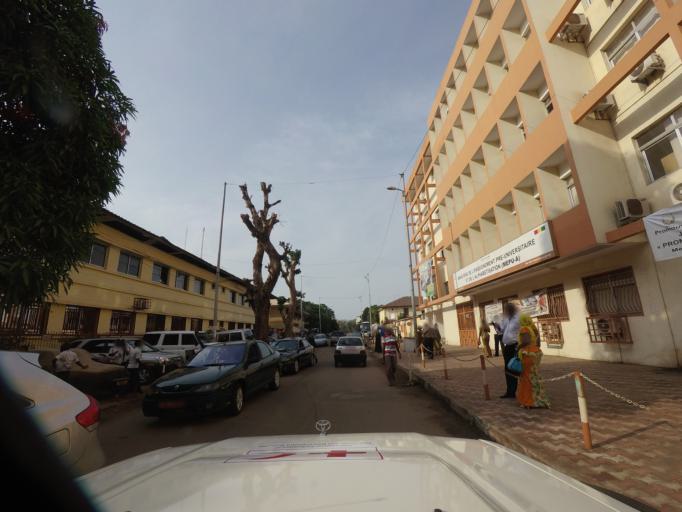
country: GN
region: Conakry
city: Camayenne
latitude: 9.5113
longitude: -13.7160
